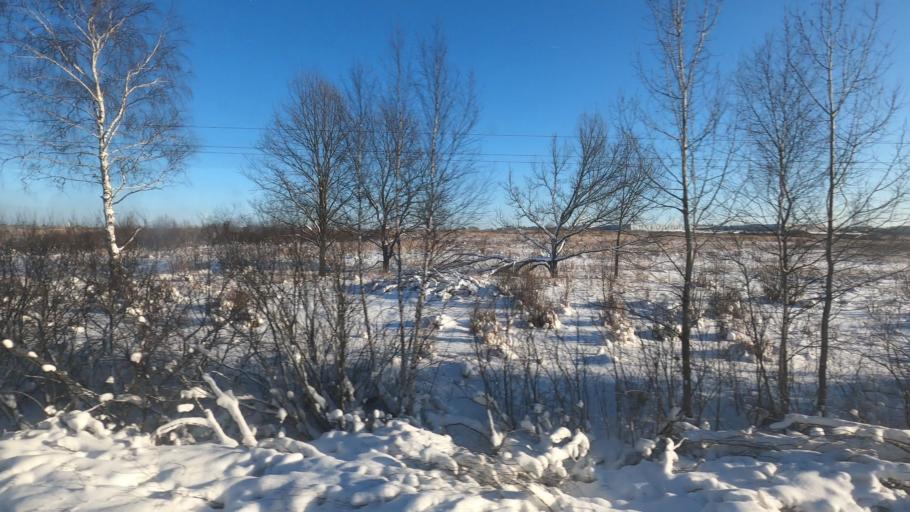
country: RU
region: Moskovskaya
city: Orud'yevo
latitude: 56.4246
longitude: 37.4981
